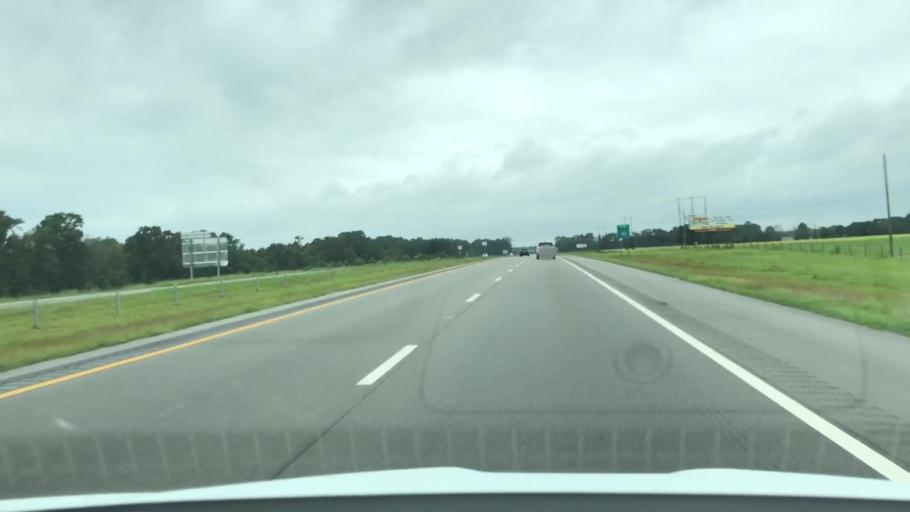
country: US
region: North Carolina
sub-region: Lenoir County
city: La Grange
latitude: 35.3134
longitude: -77.8270
